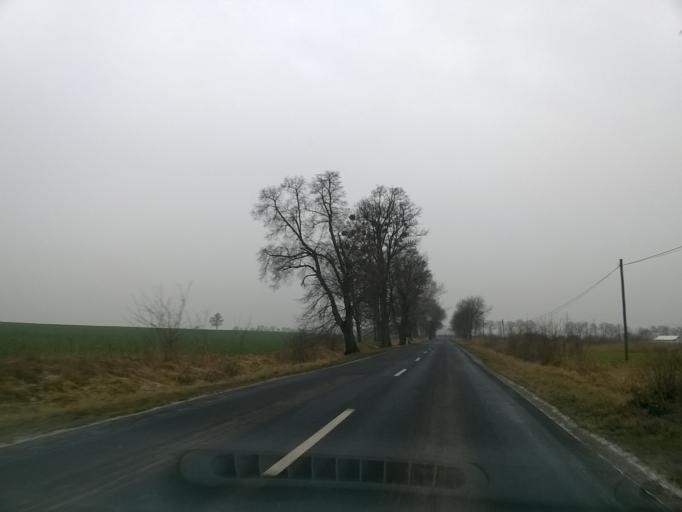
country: PL
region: Kujawsko-Pomorskie
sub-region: Powiat nakielski
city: Kcynia
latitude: 53.0114
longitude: 17.5168
